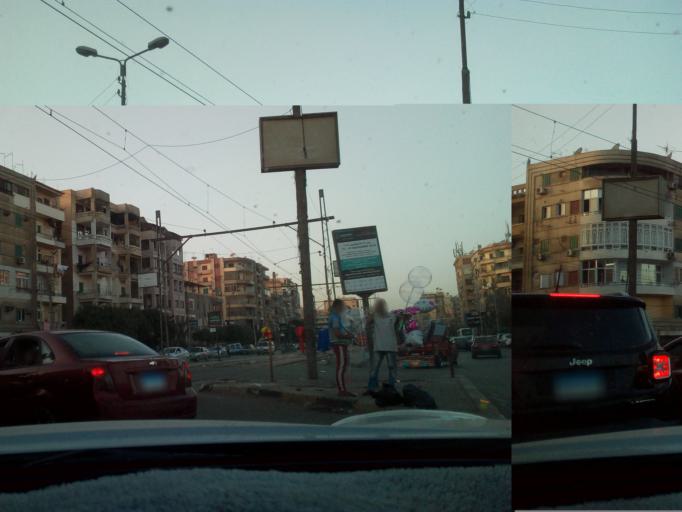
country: EG
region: Muhafazat al Qahirah
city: Cairo
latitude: 30.0973
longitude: 31.3427
